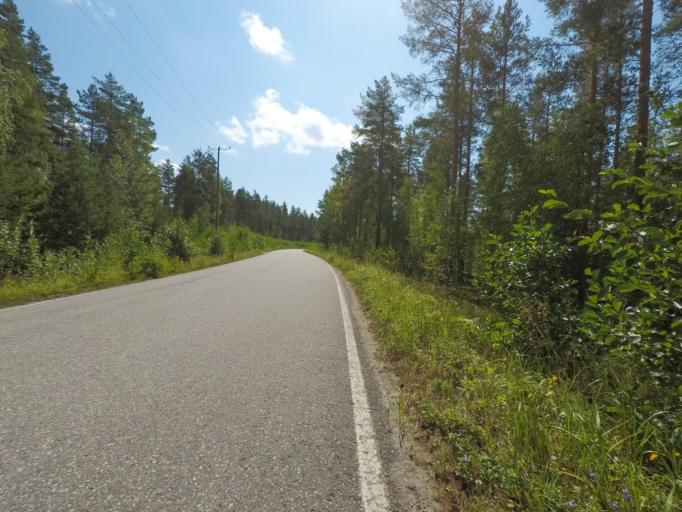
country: FI
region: Southern Savonia
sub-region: Mikkeli
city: Puumala
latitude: 61.5026
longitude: 28.1672
